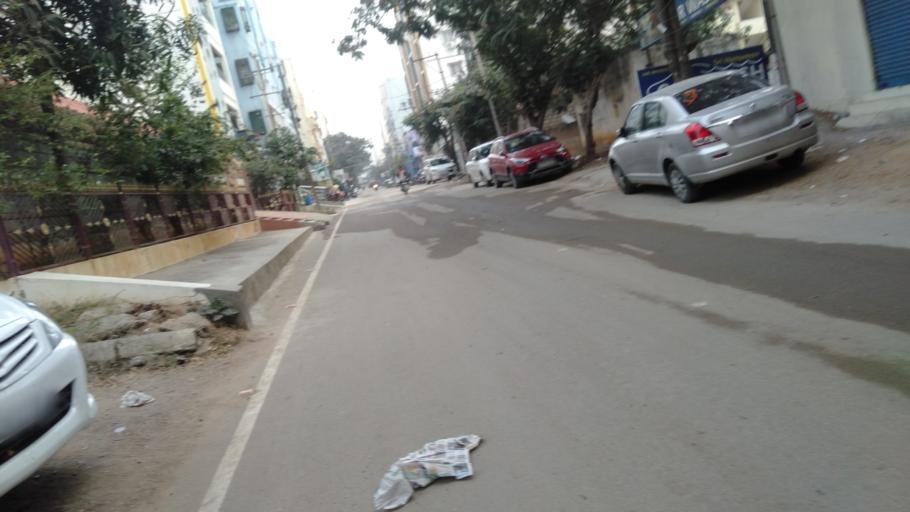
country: IN
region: Telangana
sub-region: Rangareddi
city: Kukatpalli
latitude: 17.4935
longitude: 78.3883
